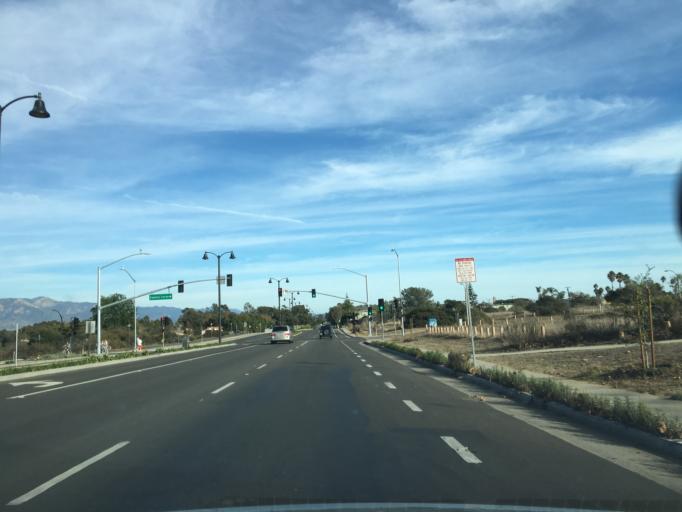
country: US
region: California
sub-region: Santa Barbara County
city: Isla Vista
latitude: 34.4173
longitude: -119.8676
